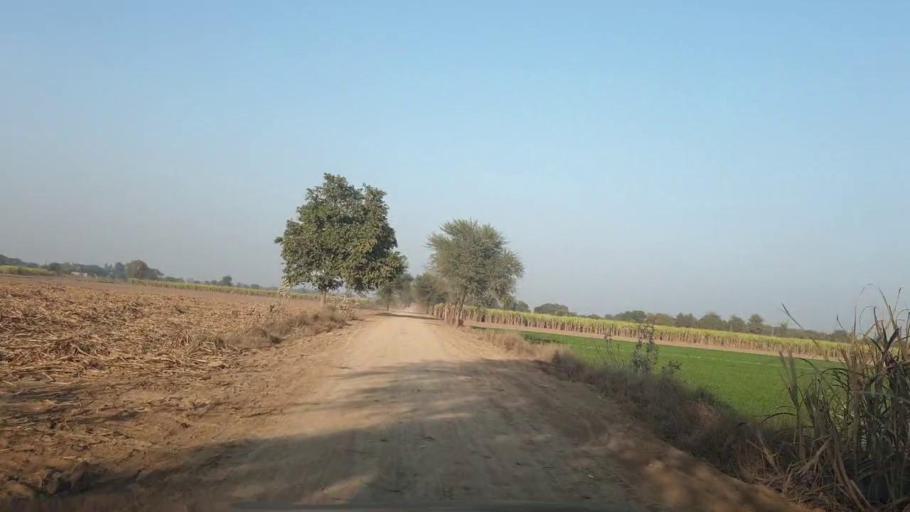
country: PK
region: Sindh
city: Ubauro
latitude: 28.3015
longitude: 69.8034
